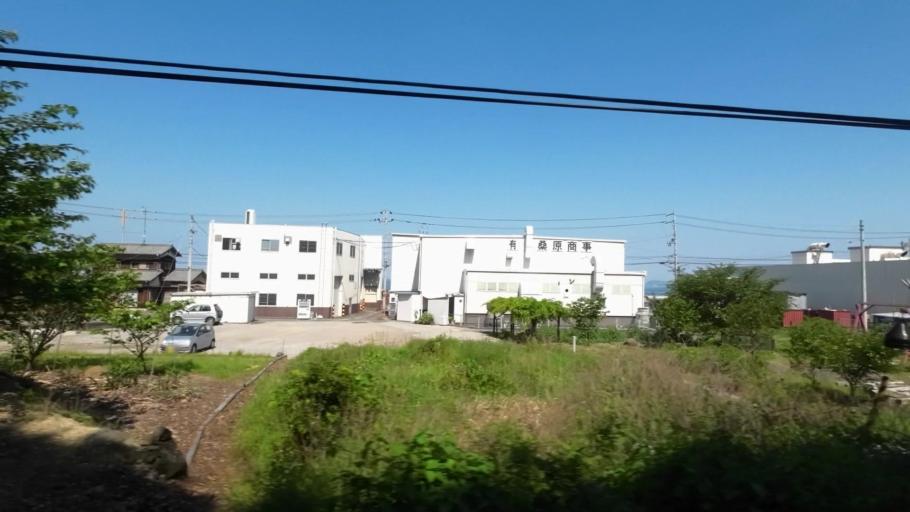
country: JP
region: Ehime
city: Kawanoecho
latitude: 34.0372
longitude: 133.5959
